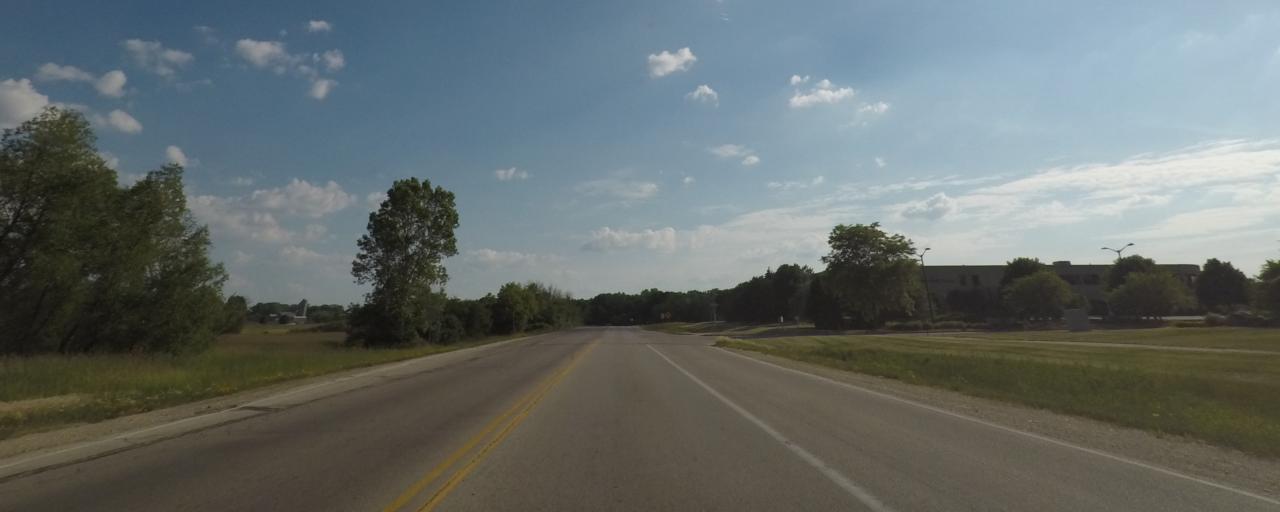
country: US
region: Wisconsin
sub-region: Waukesha County
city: New Berlin
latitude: 42.9399
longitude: -88.1106
